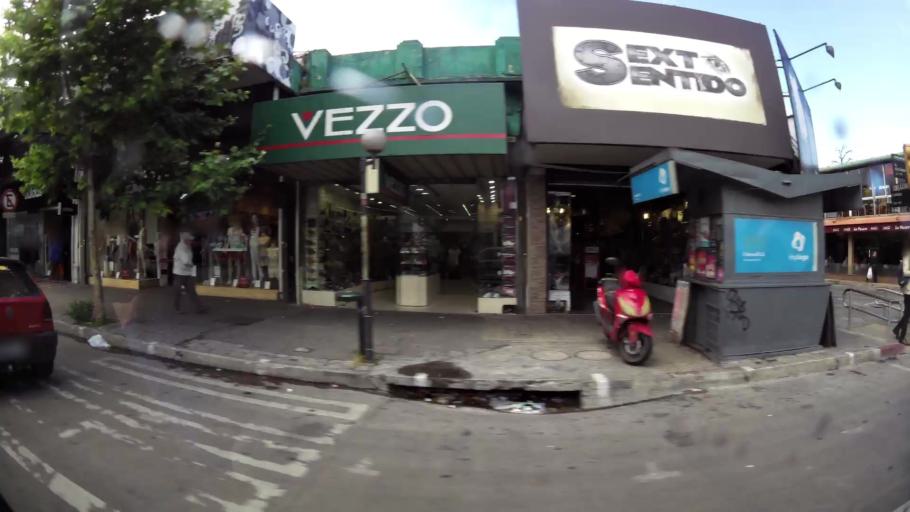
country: UY
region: Montevideo
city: Montevideo
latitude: -34.8764
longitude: -56.1428
